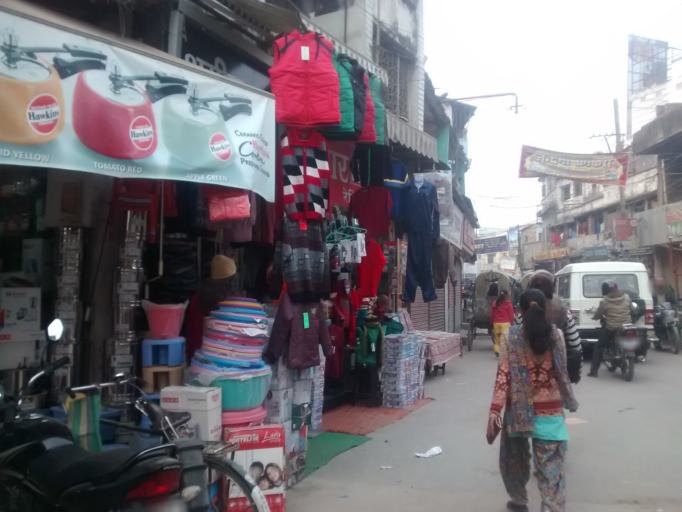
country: IN
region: Bihar
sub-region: Muzaffarpur
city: Muzaffarpur
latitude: 26.1189
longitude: 85.3916
